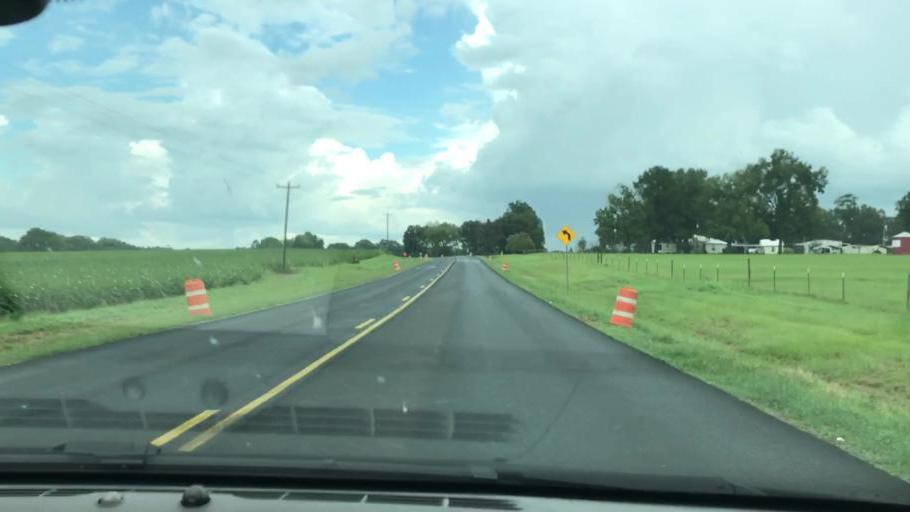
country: US
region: Georgia
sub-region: Early County
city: Blakely
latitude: 31.4261
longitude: -84.9673
